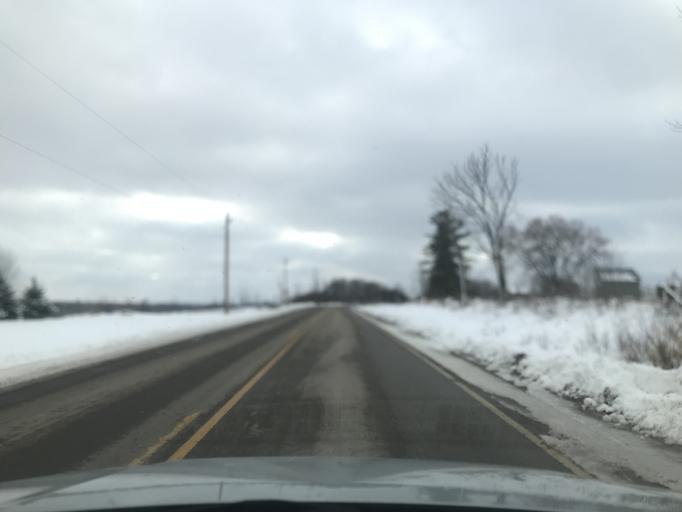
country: US
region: Wisconsin
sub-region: Oconto County
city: Oconto
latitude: 44.9371
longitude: -87.9871
